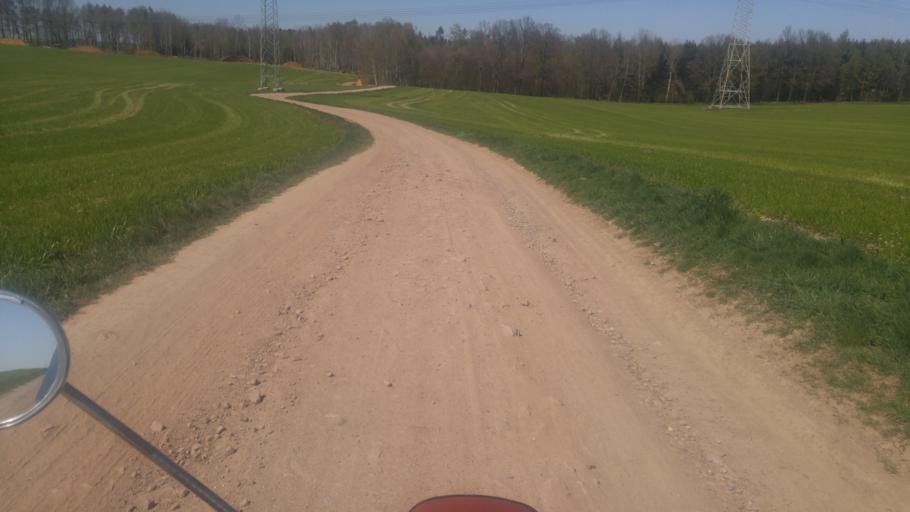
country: DE
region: Saxony
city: Altmittweida
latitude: 50.9473
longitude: 12.9629
